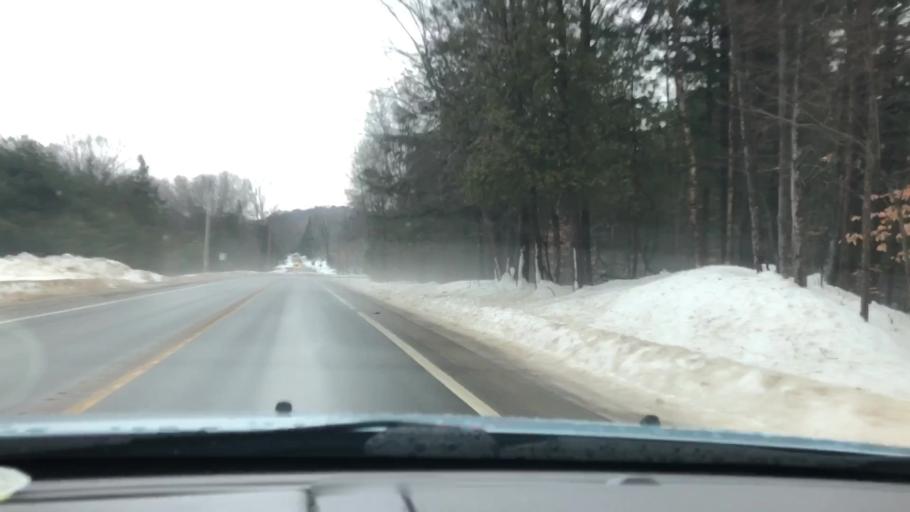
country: US
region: Michigan
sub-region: Charlevoix County
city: East Jordan
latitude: 45.1324
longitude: -85.0842
